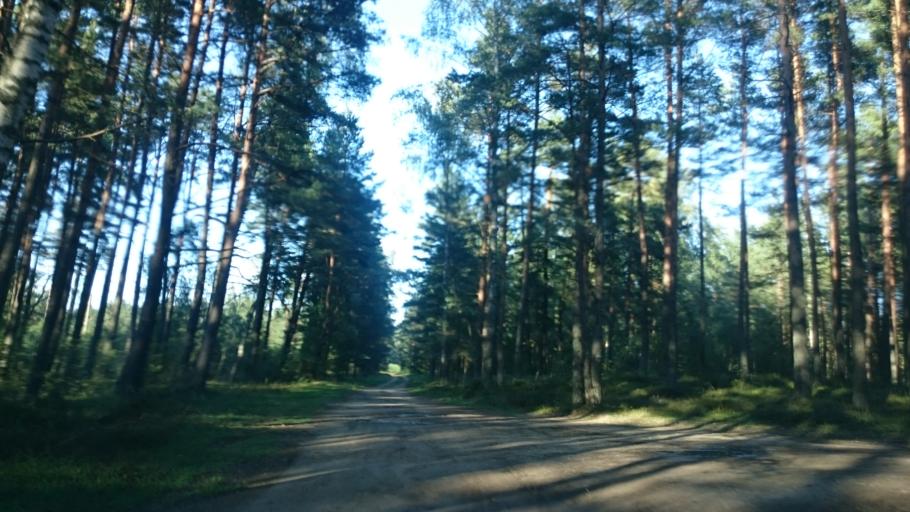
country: LV
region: Carnikava
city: Carnikava
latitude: 57.1122
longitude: 24.2415
